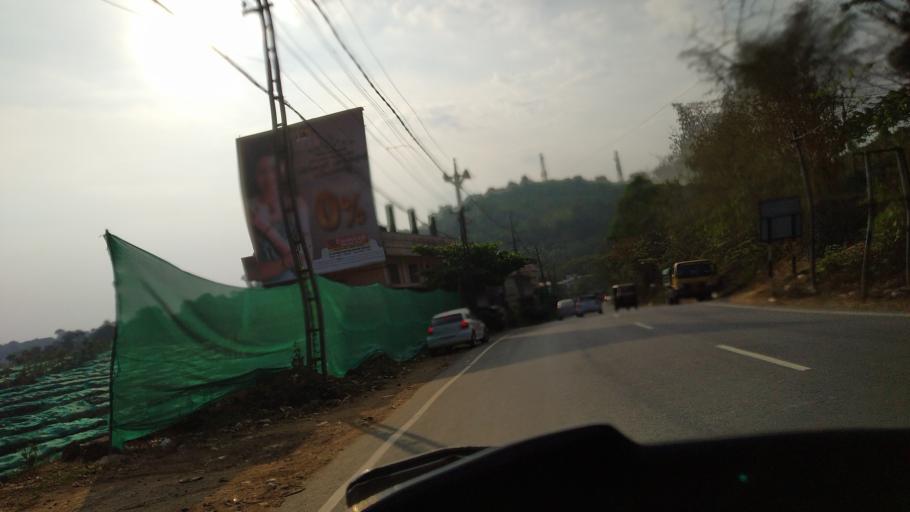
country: IN
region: Kerala
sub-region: Kottayam
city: Erattupetta
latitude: 9.5605
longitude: 76.8102
